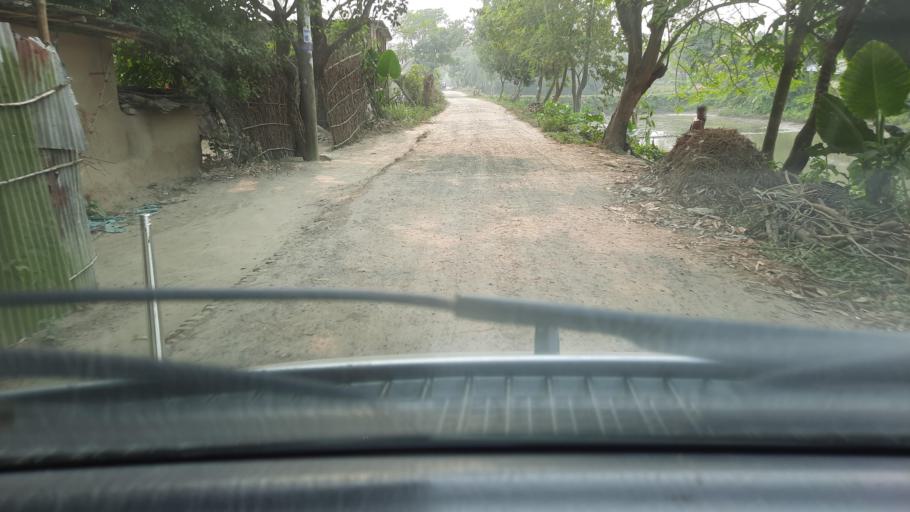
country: BD
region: Khulna
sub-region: Chuadanga
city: Nowlamary
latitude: 23.6054
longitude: 88.8597
